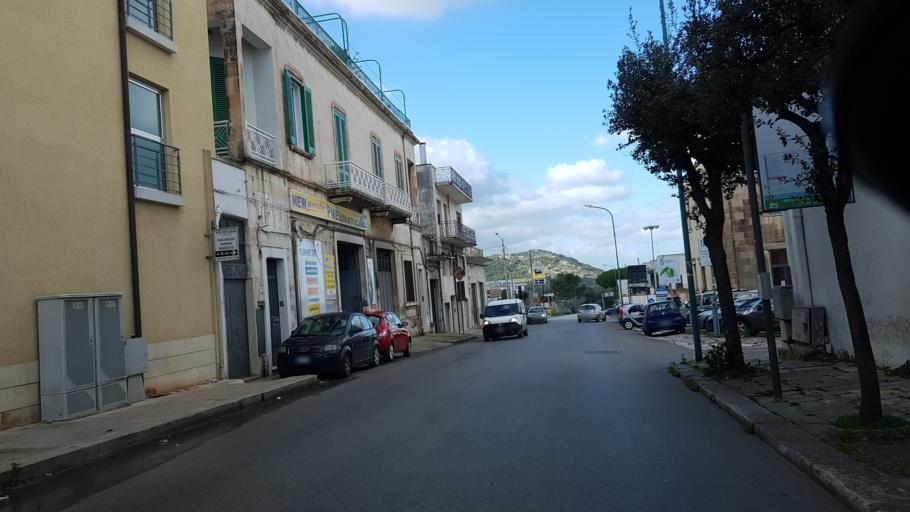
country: IT
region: Apulia
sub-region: Provincia di Brindisi
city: Ostuni
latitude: 40.7322
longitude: 17.5695
